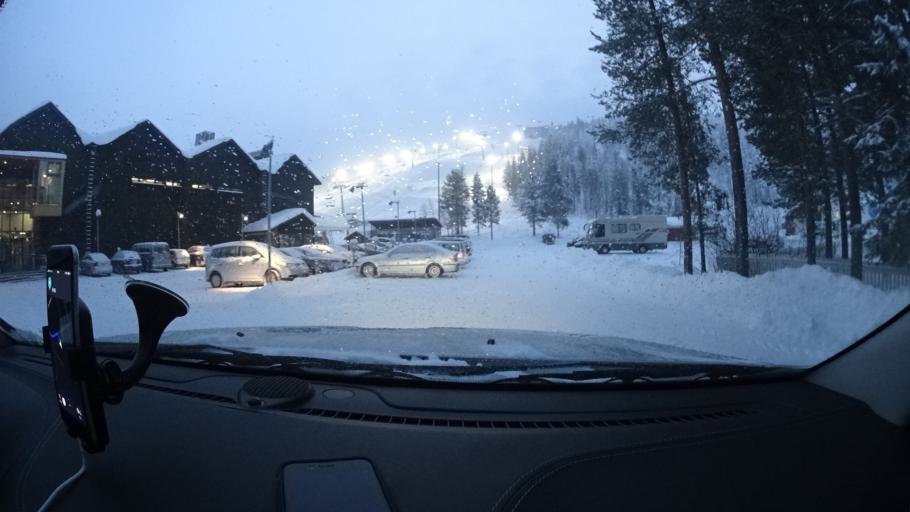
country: FI
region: Lapland
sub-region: Tunturi-Lappi
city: Kittilae
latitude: 67.8041
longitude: 24.8070
